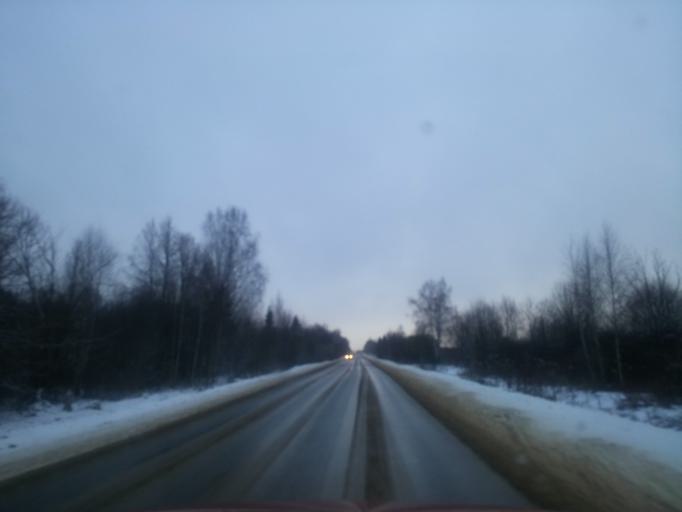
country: RU
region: Tverskaya
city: Likhoslavl'
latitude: 57.0153
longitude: 35.4589
